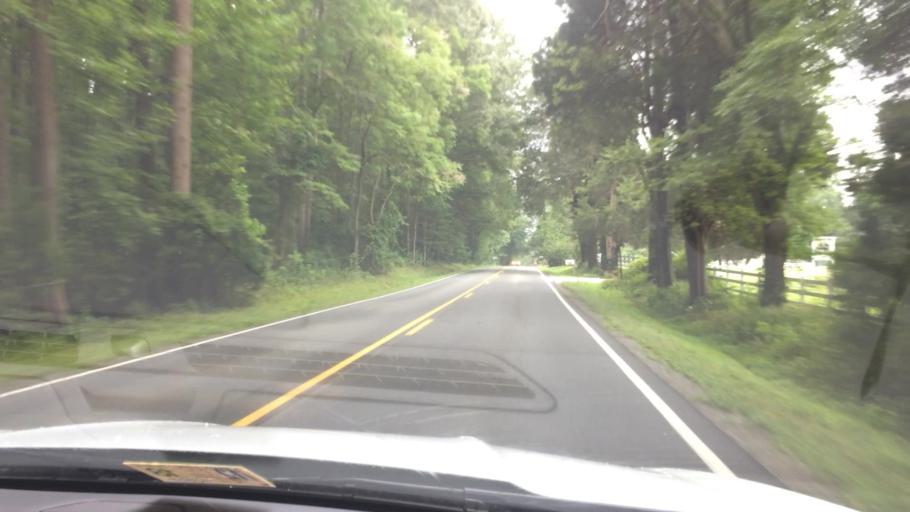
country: US
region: Virginia
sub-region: New Kent County
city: New Kent
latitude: 37.4610
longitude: -77.0352
